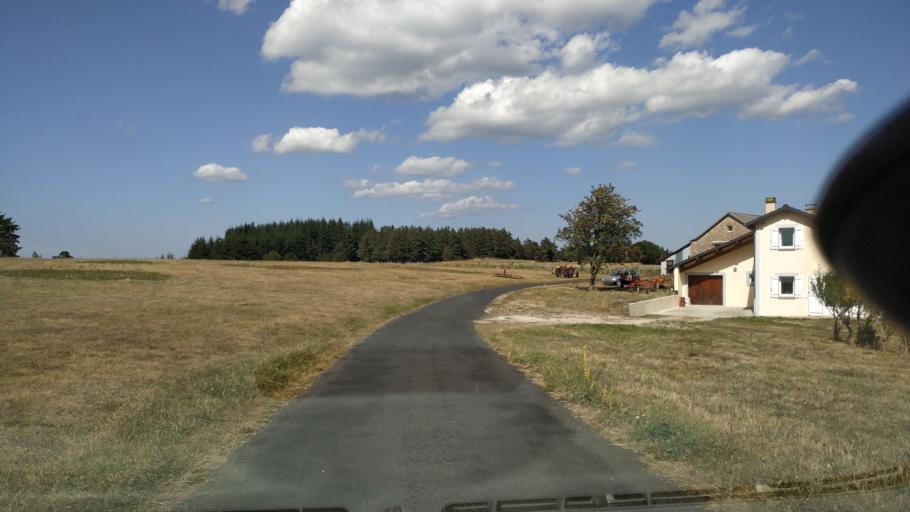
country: FR
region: Rhone-Alpes
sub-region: Departement de l'Ardeche
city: Saint-Agreve
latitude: 45.0303
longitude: 4.4445
